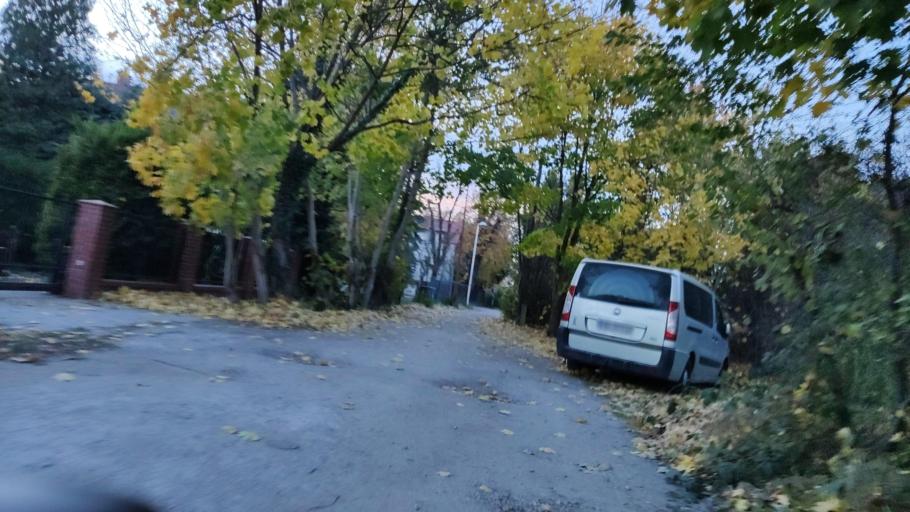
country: PL
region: Lower Silesian Voivodeship
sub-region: Powiat wroclawski
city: Radwanice
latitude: 51.0643
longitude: 17.0751
